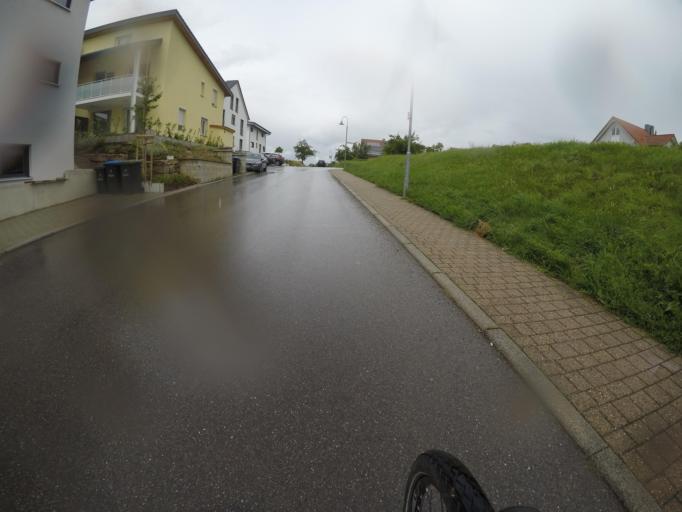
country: DE
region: Baden-Wuerttemberg
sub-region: Regierungsbezirk Stuttgart
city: Bondorf
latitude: 48.5270
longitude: 8.8294
